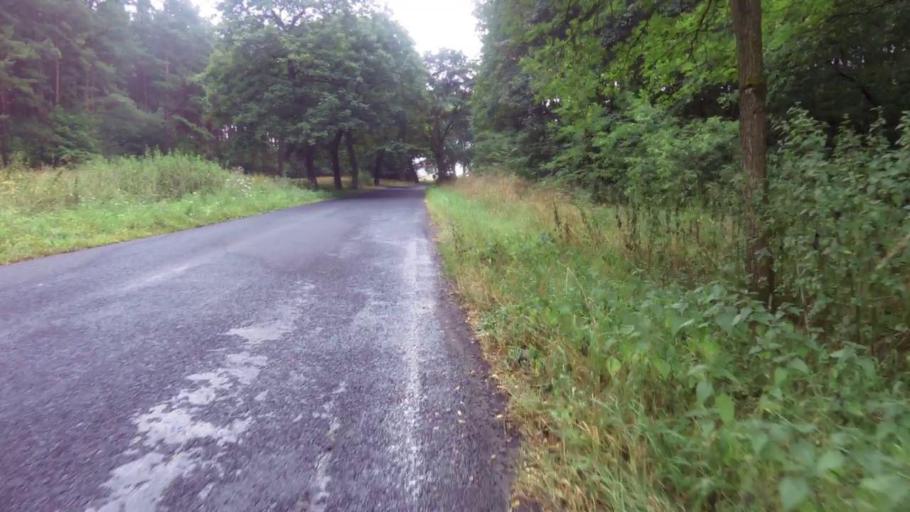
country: PL
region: West Pomeranian Voivodeship
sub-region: Powiat choszczenski
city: Choszczno
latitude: 53.2188
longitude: 15.3880
